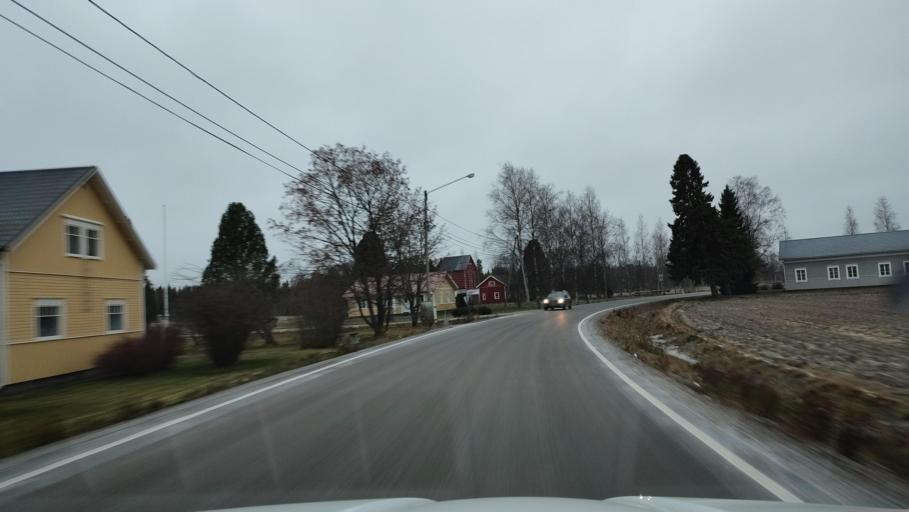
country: FI
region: Southern Ostrobothnia
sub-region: Suupohja
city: Karijoki
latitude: 62.2384
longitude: 21.5773
